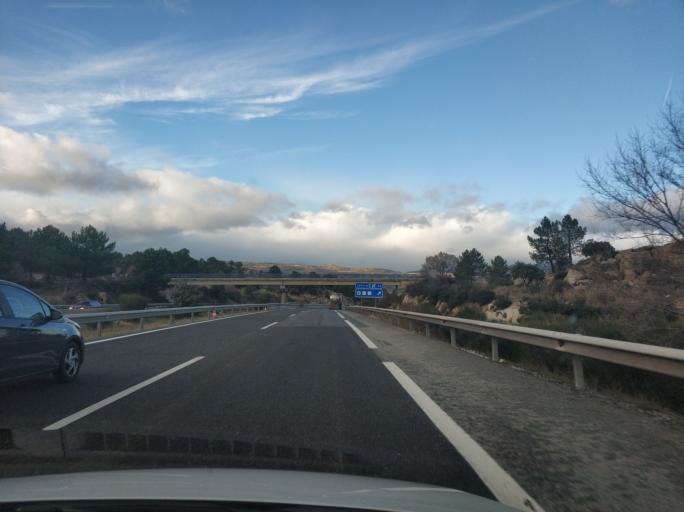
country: ES
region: Madrid
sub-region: Provincia de Madrid
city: La Cabrera
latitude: 40.8902
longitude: -3.6009
